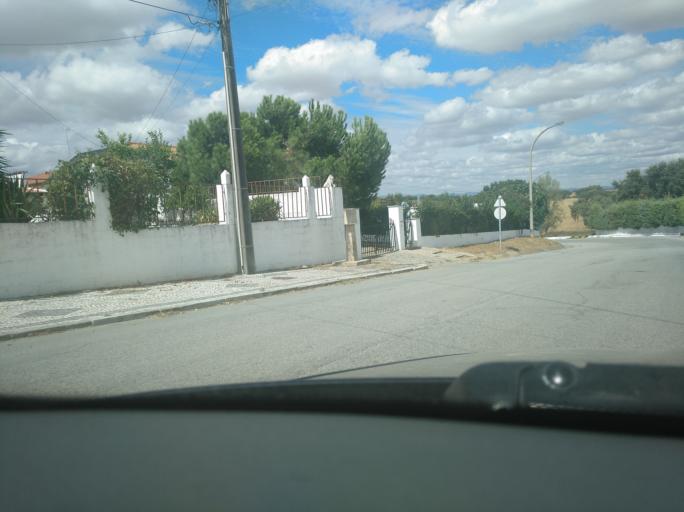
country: PT
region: Portalegre
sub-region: Arronches
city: Arronches
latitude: 39.0557
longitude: -7.4353
